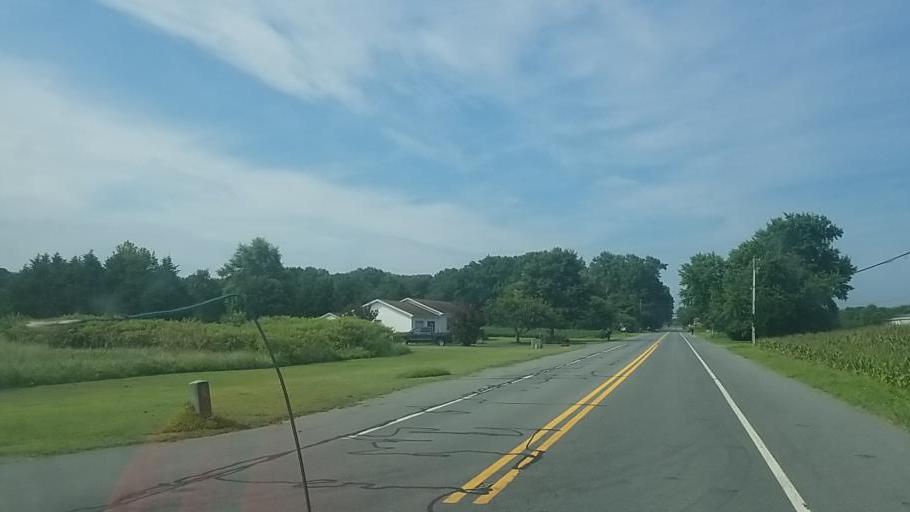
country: US
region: Delaware
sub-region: Sussex County
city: Long Neck
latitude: 38.5408
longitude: -75.1811
